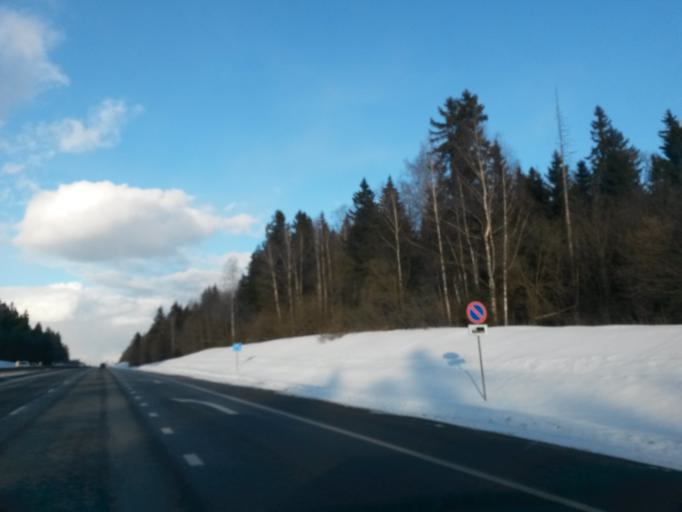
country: RU
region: Moskovskaya
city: Sergiyev Posad
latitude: 56.2267
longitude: 38.1226
